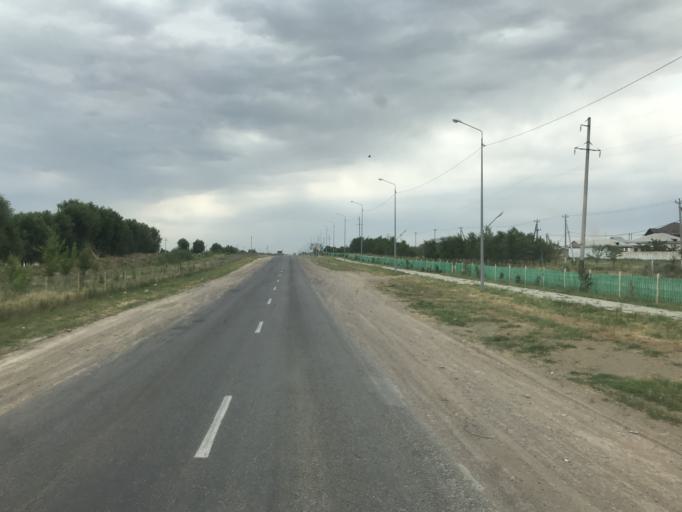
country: KZ
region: Ongtustik Qazaqstan
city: Saryaghash
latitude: 41.4199
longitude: 69.0877
